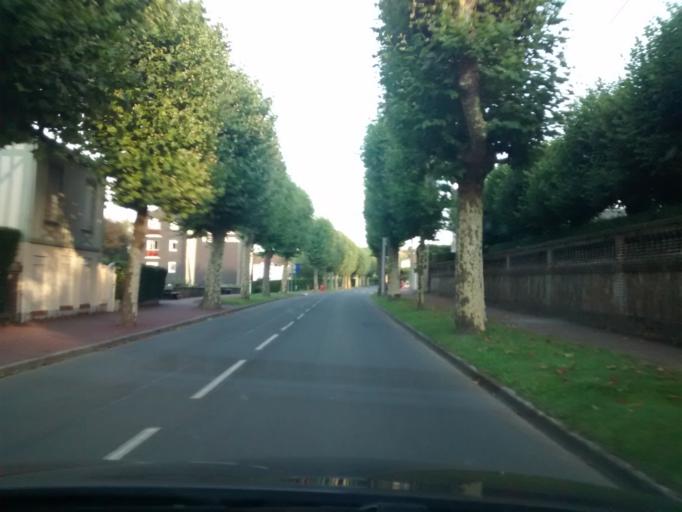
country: FR
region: Lower Normandy
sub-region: Departement du Calvados
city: Villers-sur-Mer
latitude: 49.3202
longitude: 0.0002
